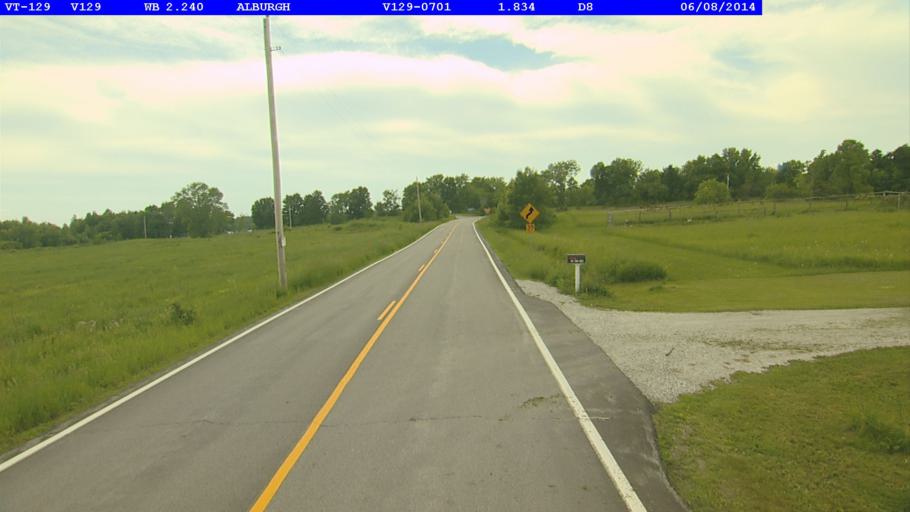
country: US
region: Vermont
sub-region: Grand Isle County
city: North Hero
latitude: 44.8874
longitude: -73.2980
